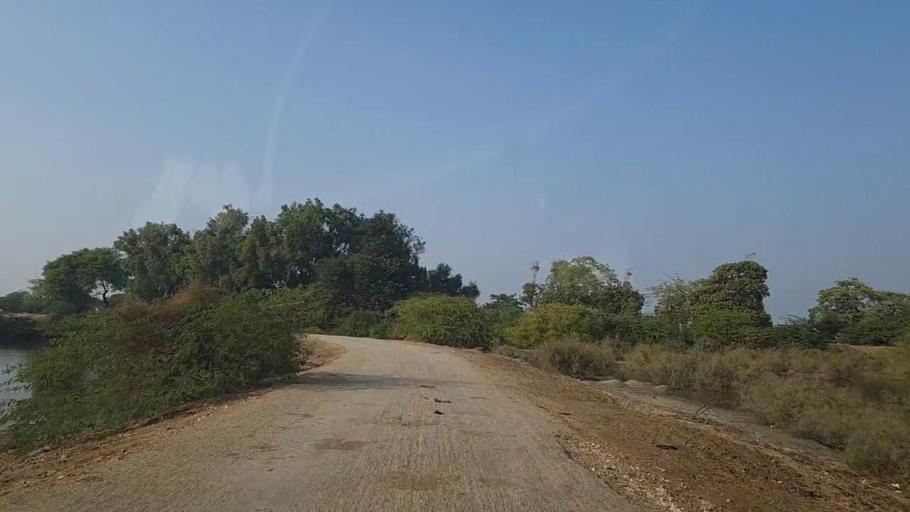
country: PK
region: Sindh
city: Mirpur Sakro
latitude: 24.5733
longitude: 67.6658
